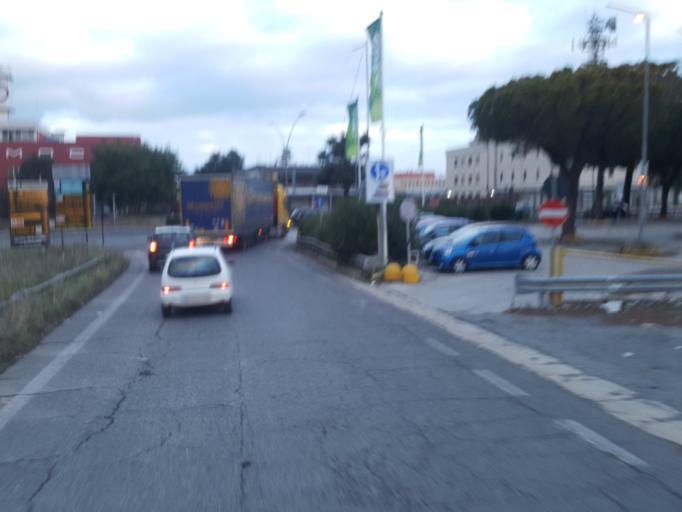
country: IT
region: Latium
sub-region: Citta metropolitana di Roma Capitale
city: Area Produttiva
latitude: 41.6771
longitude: 12.5004
